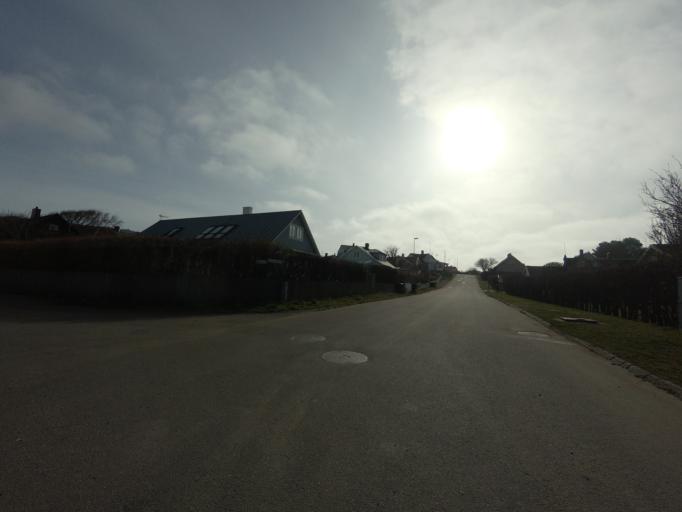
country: SE
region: Skane
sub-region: Hoganas Kommun
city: Hoganas
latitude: 56.2806
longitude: 12.4961
